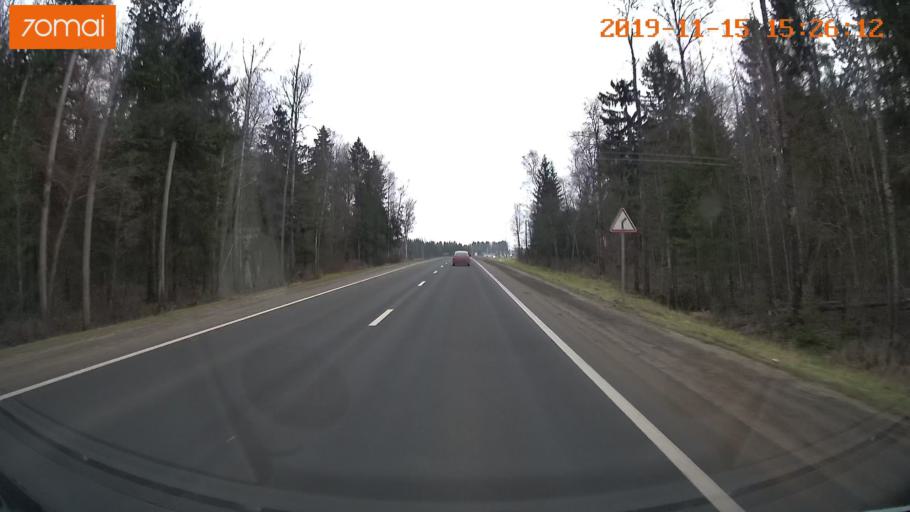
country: RU
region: Jaroslavl
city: Danilov
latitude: 58.1548
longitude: 40.1457
